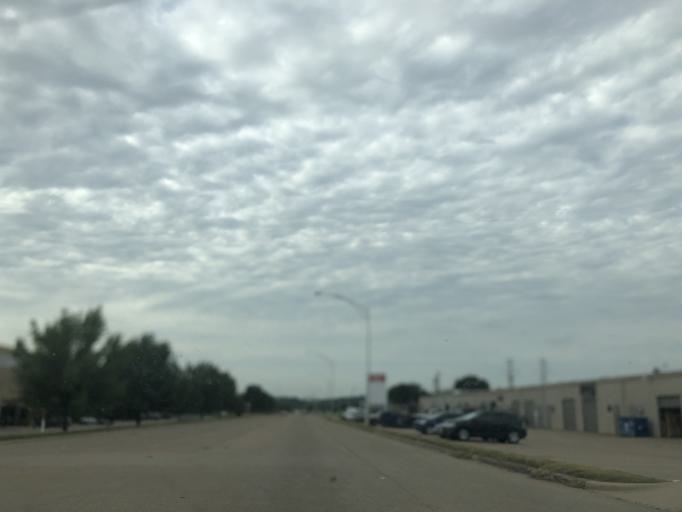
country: US
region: Texas
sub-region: Tarrant County
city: Richland Hills
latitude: 32.7908
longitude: -97.2212
